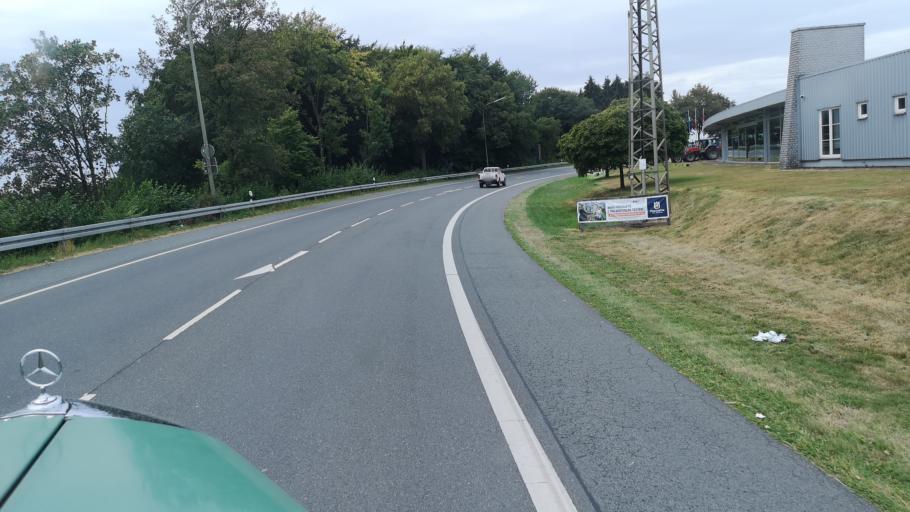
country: DE
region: North Rhine-Westphalia
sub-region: Regierungsbezirk Koln
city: Kurten
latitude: 51.0445
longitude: 7.2259
